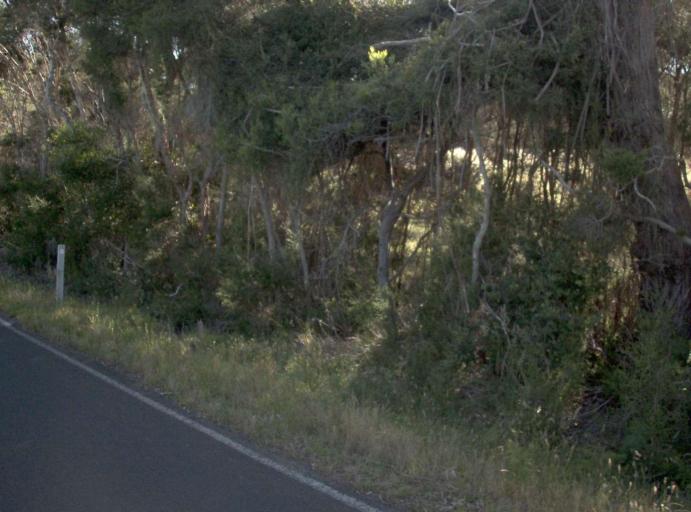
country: AU
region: Victoria
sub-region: Latrobe
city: Morwell
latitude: -38.7015
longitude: 146.3986
